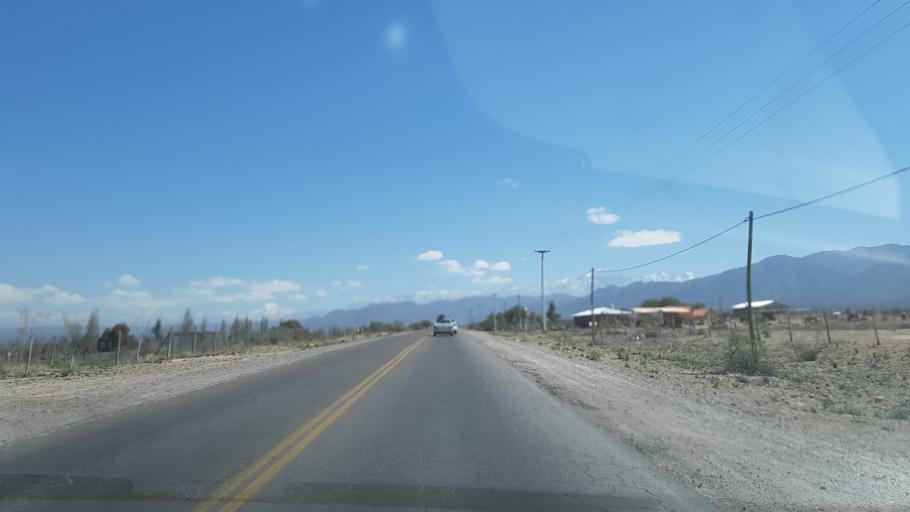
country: AR
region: Mendoza
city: Lujan de Cuyo
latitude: -33.0177
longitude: -68.9395
